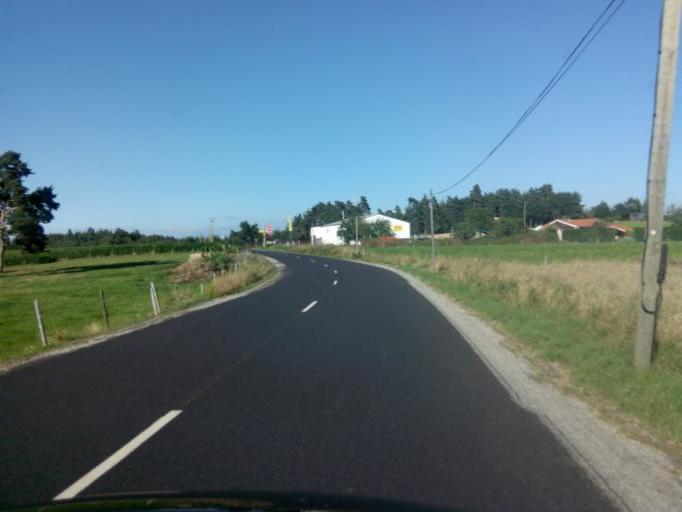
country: FR
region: Rhone-Alpes
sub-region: Departement de la Loire
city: Usson-en-Forez
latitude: 45.3531
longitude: 3.9880
